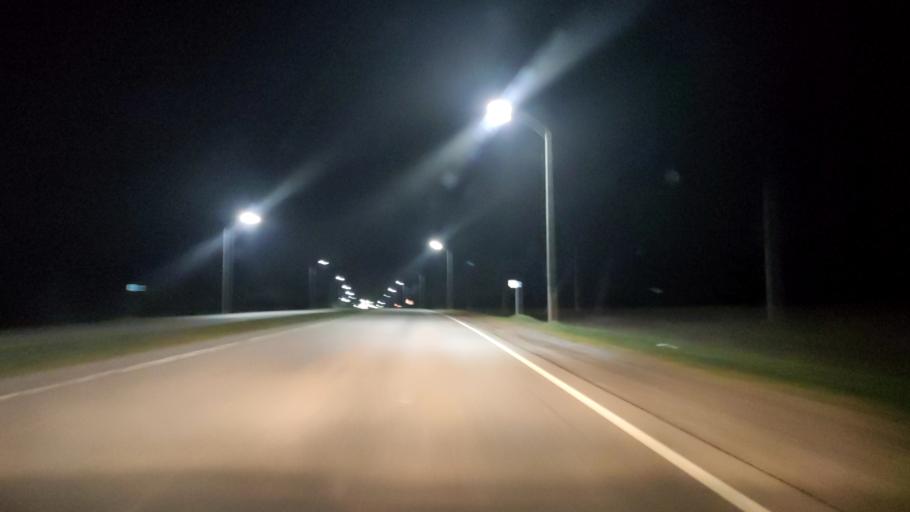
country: RU
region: Belgorod
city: Staryy Oskol
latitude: 51.3951
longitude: 37.8712
